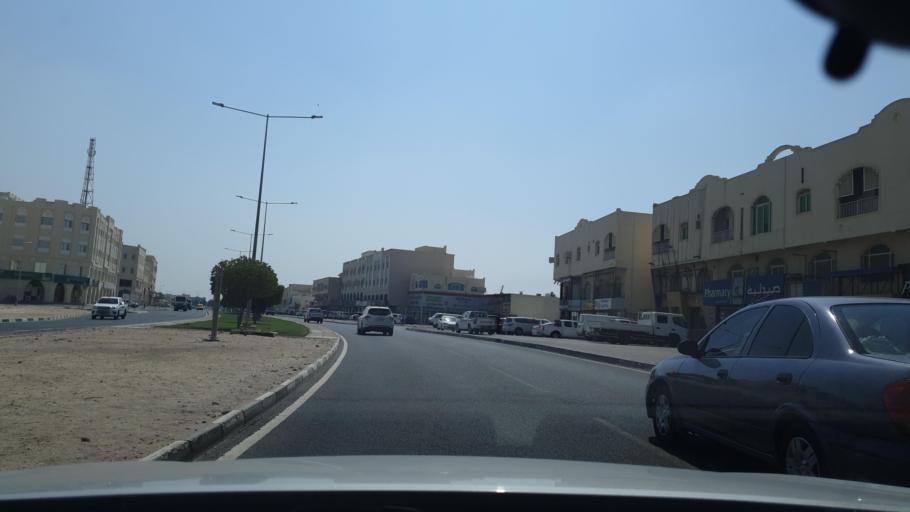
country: QA
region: Al Khawr
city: Al Khawr
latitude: 25.6864
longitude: 51.4952
